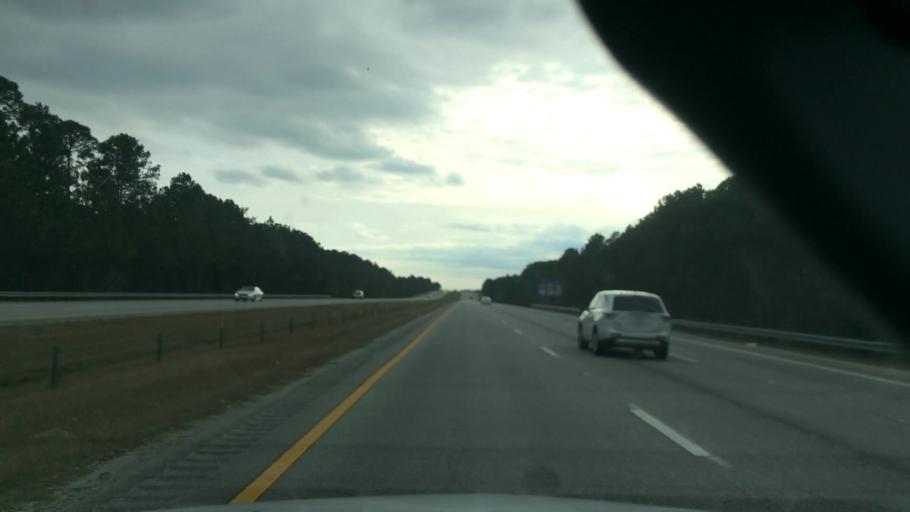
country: US
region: South Carolina
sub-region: Horry County
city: North Myrtle Beach
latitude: 33.8602
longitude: -78.6958
